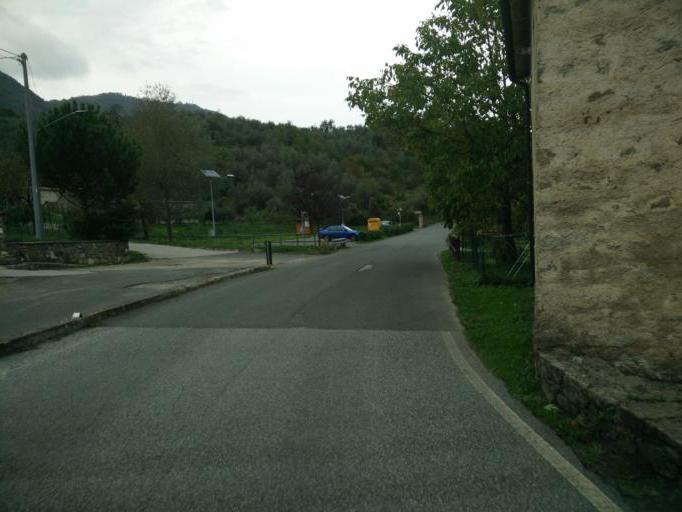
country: IT
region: Tuscany
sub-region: Provincia di Massa-Carrara
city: Casola in Lunigiana
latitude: 44.1935
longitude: 10.1511
